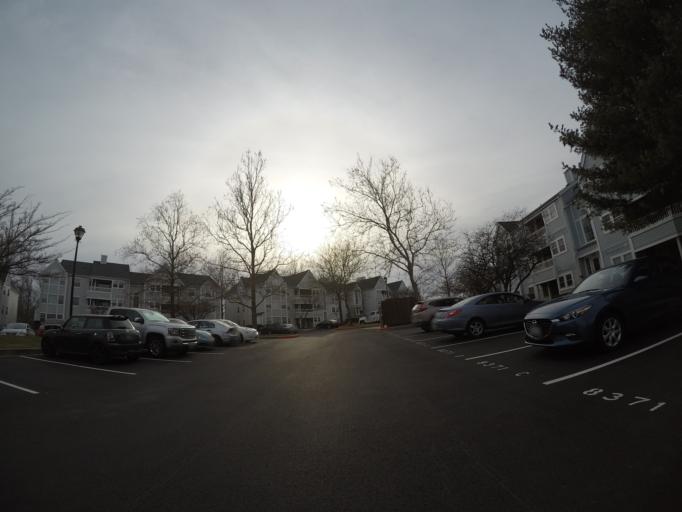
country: US
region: Maryland
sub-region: Howard County
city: Columbia
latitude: 39.2183
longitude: -76.8014
